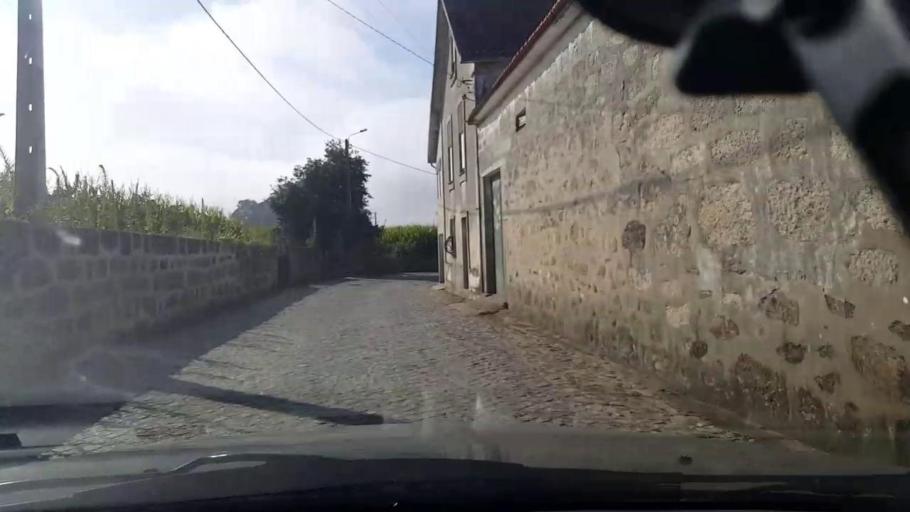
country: PT
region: Porto
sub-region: Maia
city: Gemunde
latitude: 41.2677
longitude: -8.6743
